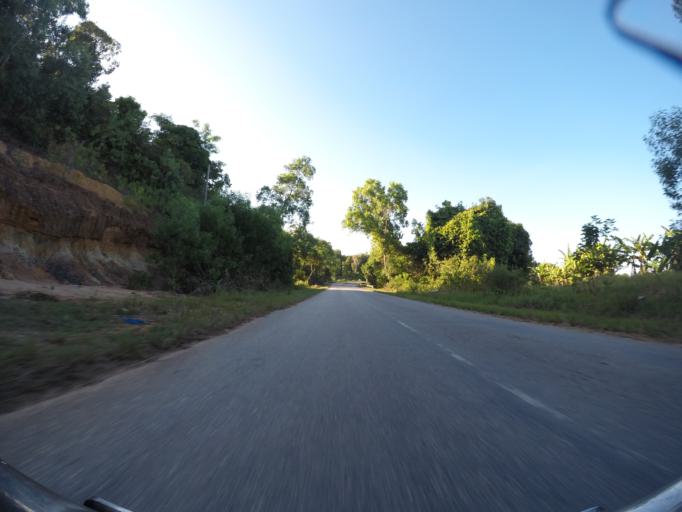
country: TZ
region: Pemba South
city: Uwelini
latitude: -5.3776
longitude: 39.6743
